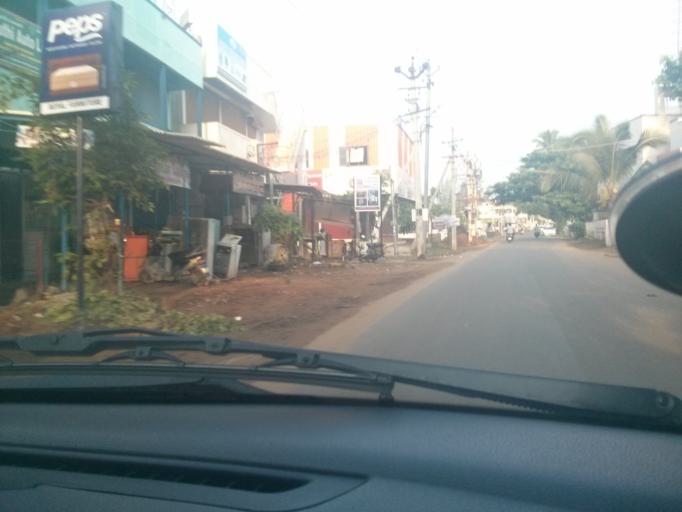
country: IN
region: Tamil Nadu
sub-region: Coimbatore
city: Coimbatore
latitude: 11.0396
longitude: 76.9322
